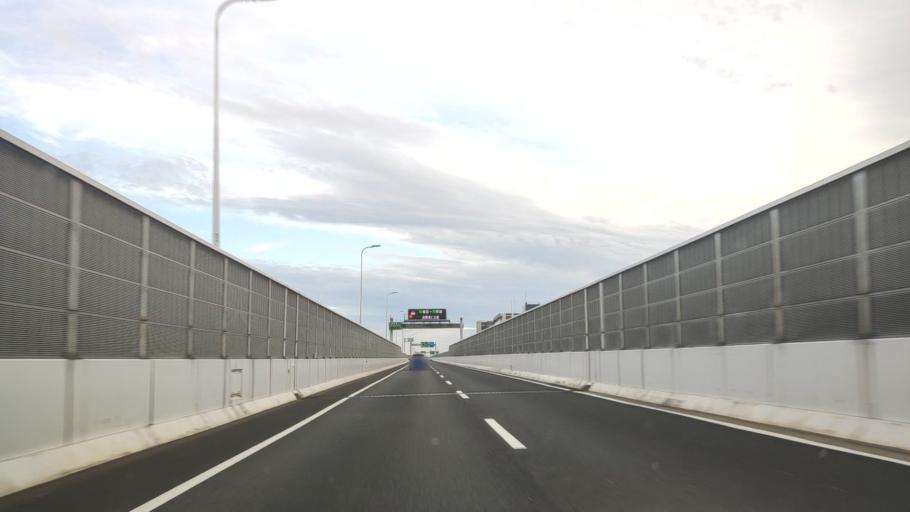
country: JP
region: Aichi
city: Nagoya-shi
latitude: 35.2014
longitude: 136.9118
